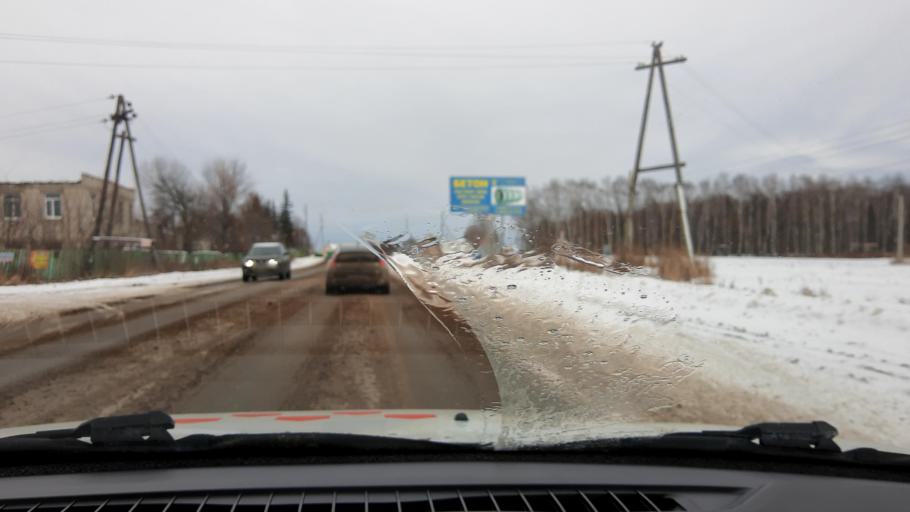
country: RU
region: Nizjnij Novgorod
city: Gorodets
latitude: 56.6440
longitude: 43.5018
